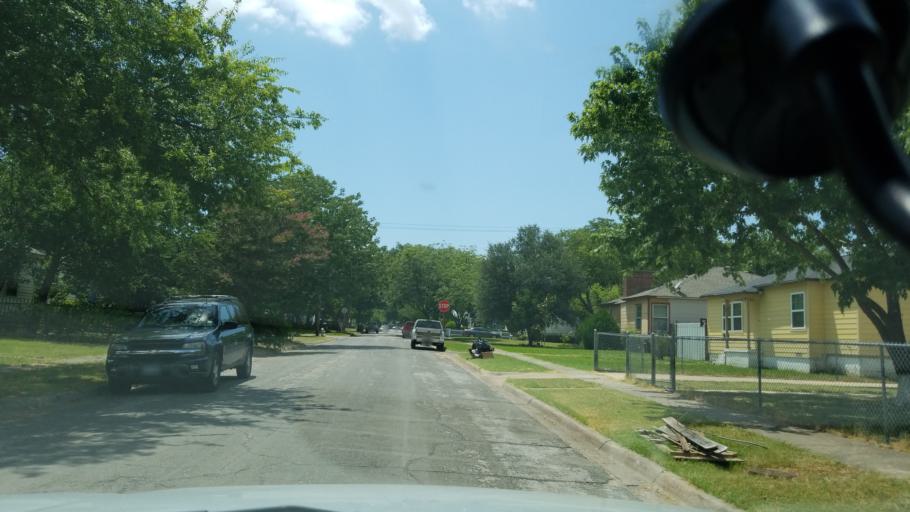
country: US
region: Texas
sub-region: Dallas County
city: Cockrell Hill
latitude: 32.7307
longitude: -96.8712
